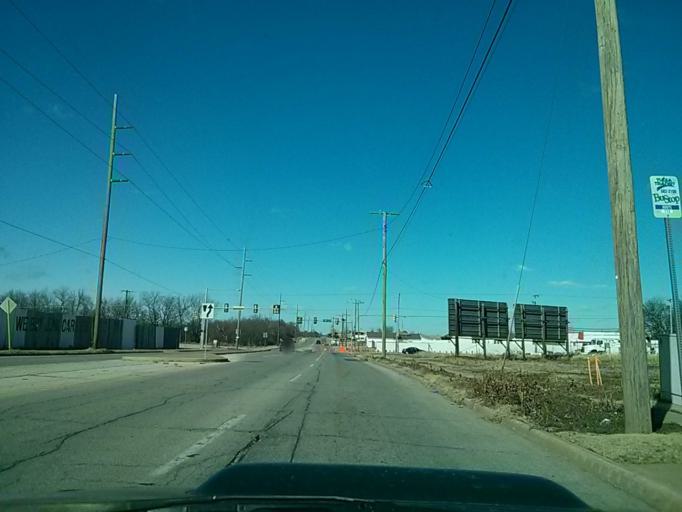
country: US
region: Oklahoma
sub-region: Tulsa County
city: Turley
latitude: 36.2051
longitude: -95.9582
